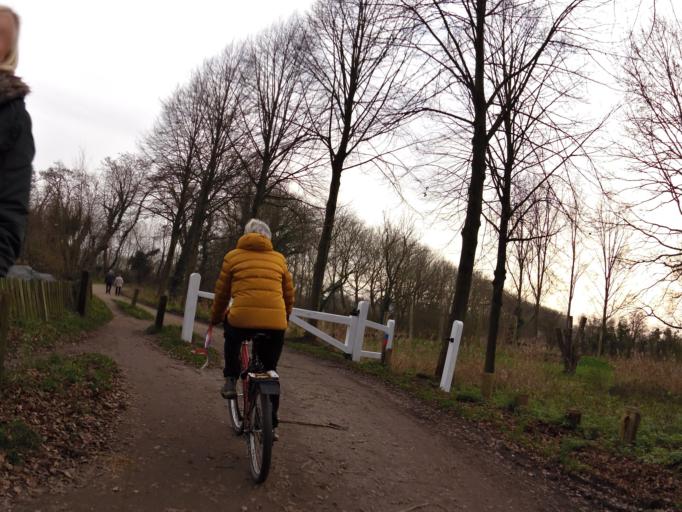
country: NL
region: North Brabant
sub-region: Gemeente Sint-Michielsgestel
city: Sint-Michielsgestel
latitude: 51.6542
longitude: 5.3226
